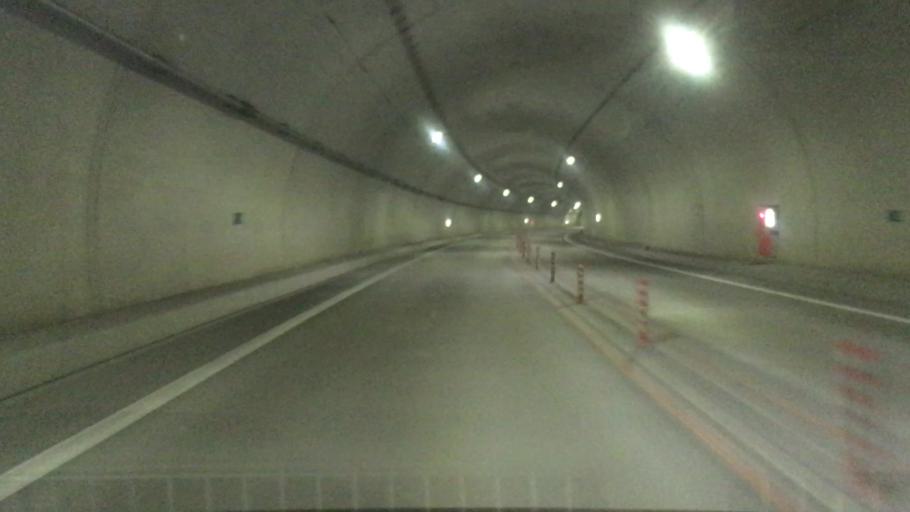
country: JP
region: Hyogo
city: Toyooka
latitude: 35.6264
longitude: 134.5203
